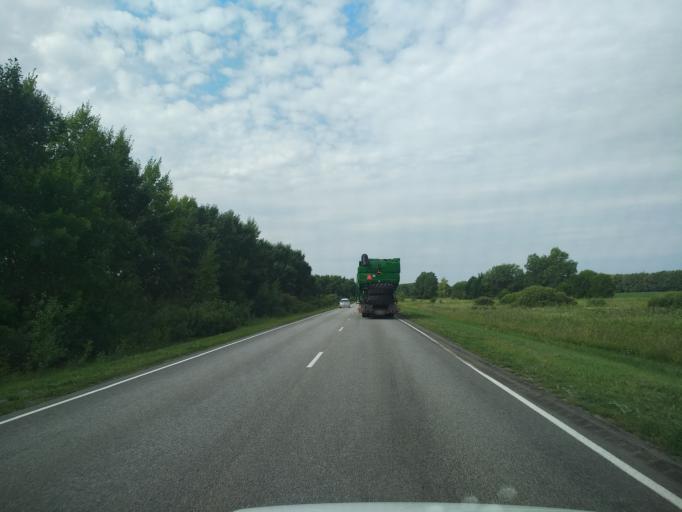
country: RU
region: Voronezj
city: Pereleshinskiy
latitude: 51.8696
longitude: 40.3852
